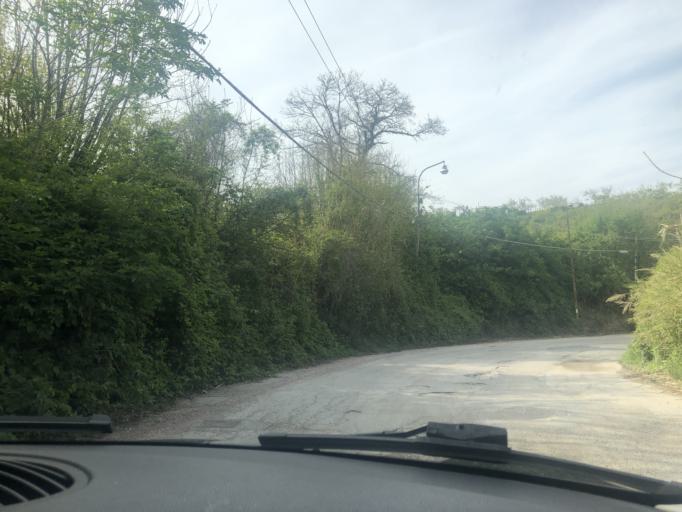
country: IT
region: Campania
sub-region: Provincia di Napoli
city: Torre Caracciolo
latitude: 40.8710
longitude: 14.1926
